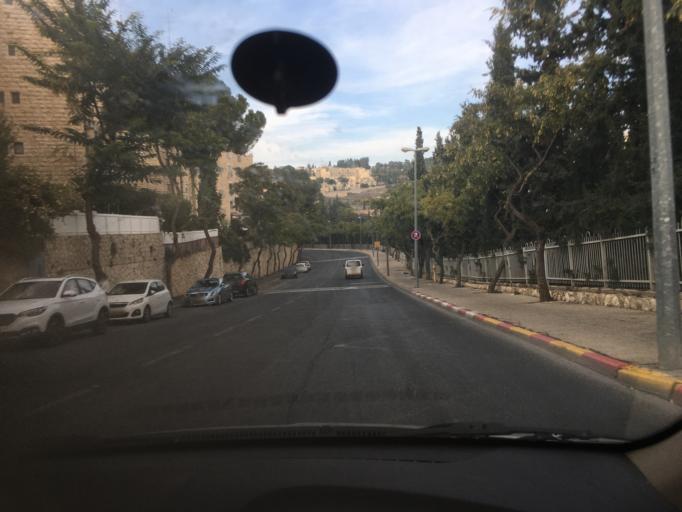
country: PS
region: West Bank
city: Ash Shaykh Sa`d
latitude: 31.7470
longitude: 35.2331
